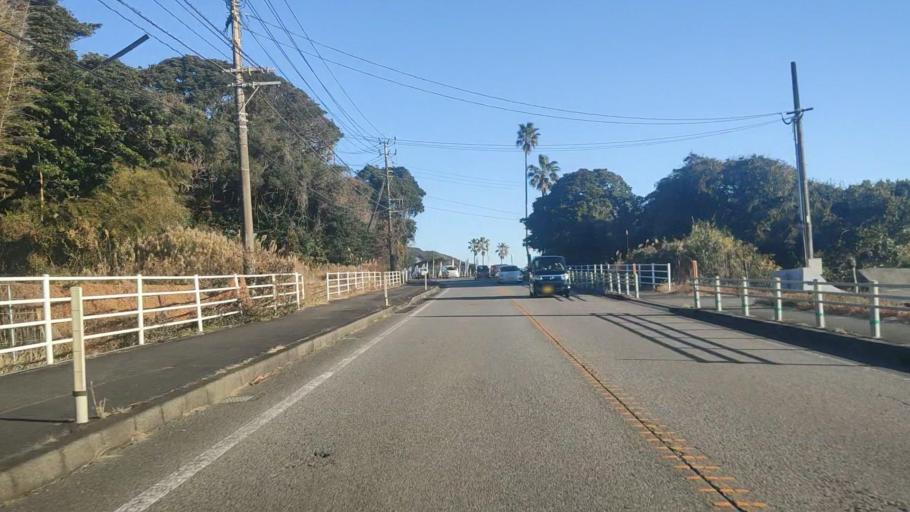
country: JP
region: Miyazaki
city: Nobeoka
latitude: 32.3575
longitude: 131.6214
